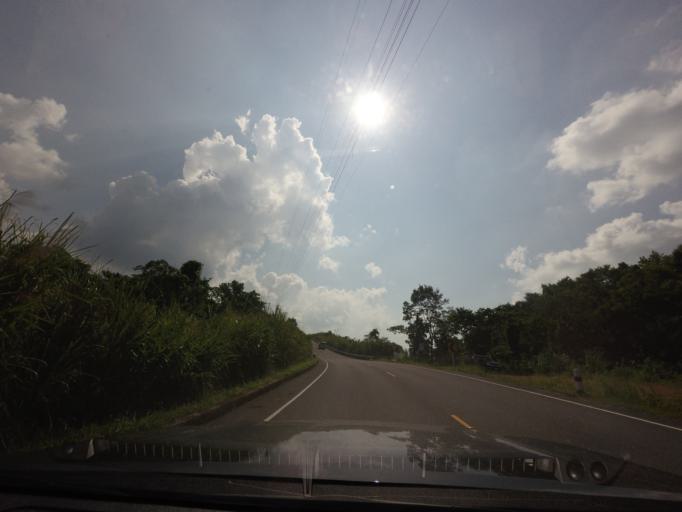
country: TH
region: Nan
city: Santi Suk
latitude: 18.9760
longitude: 101.0400
